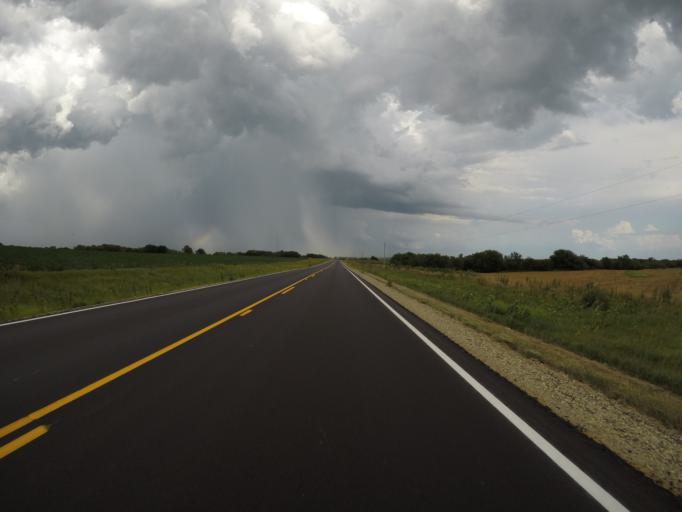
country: US
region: Kansas
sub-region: Marshall County
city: Blue Rapids
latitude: 39.4366
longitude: -96.8163
